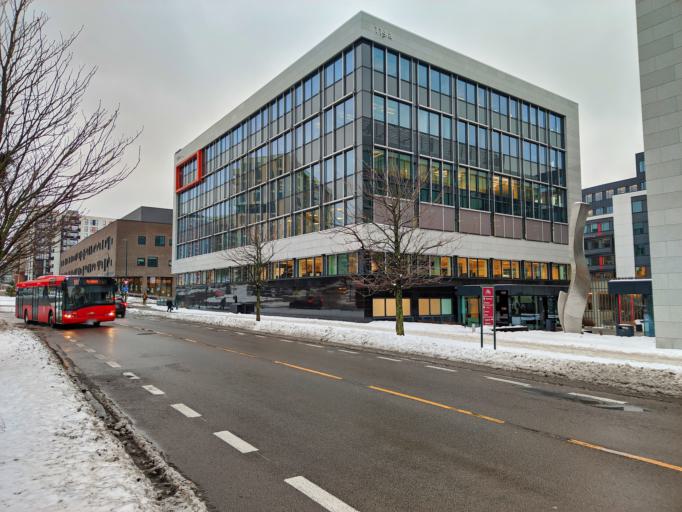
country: NO
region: Oslo
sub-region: Oslo
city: Oslo
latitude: 59.9478
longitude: 10.7706
